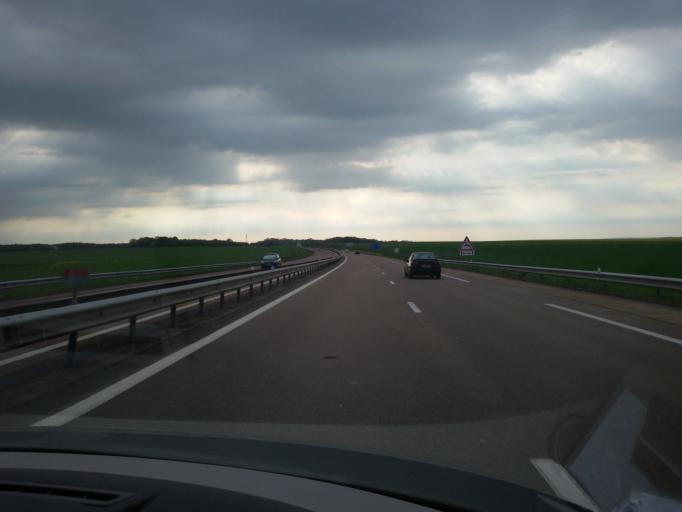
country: FR
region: Champagne-Ardenne
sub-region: Departement de la Haute-Marne
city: Chamarandes-Choignes
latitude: 48.0411
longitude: 5.0510
